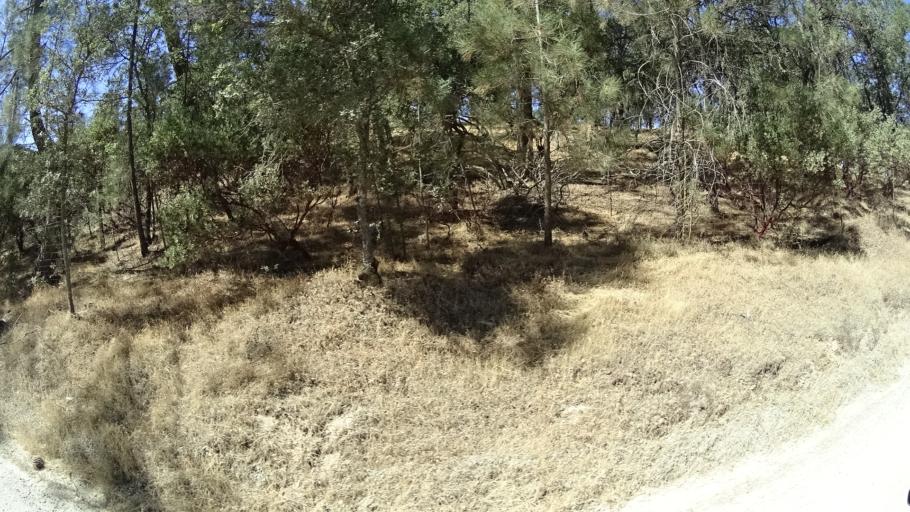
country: US
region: California
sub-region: Calaveras County
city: Valley Springs
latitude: 38.2168
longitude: -120.8687
